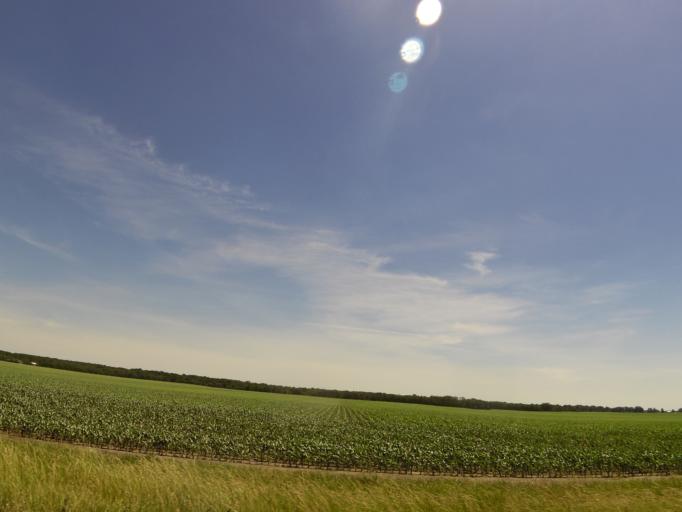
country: US
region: Illinois
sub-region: Vermilion County
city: Rossville
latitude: 40.3144
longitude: -87.6588
